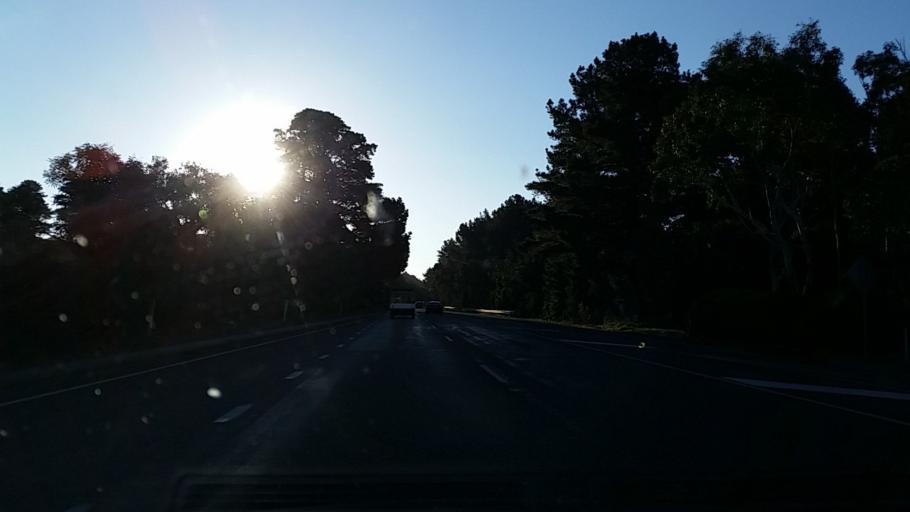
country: AU
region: South Australia
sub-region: Alexandrina
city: Mount Compass
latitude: -35.3383
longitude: 138.5968
